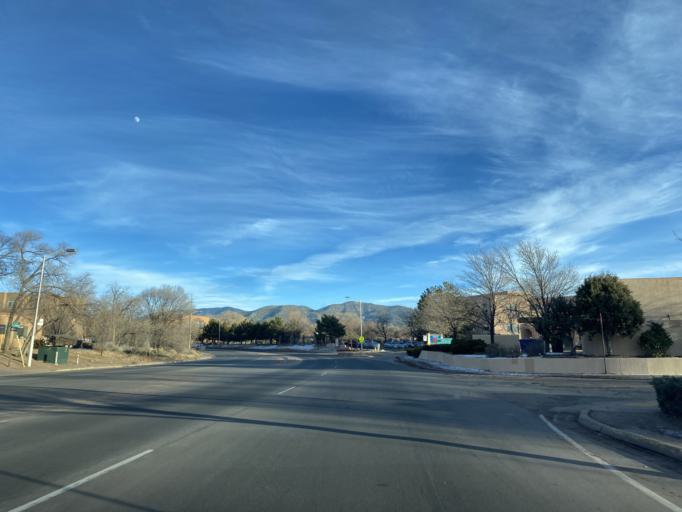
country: US
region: New Mexico
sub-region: Santa Fe County
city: Santa Fe
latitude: 35.6921
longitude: -105.9457
